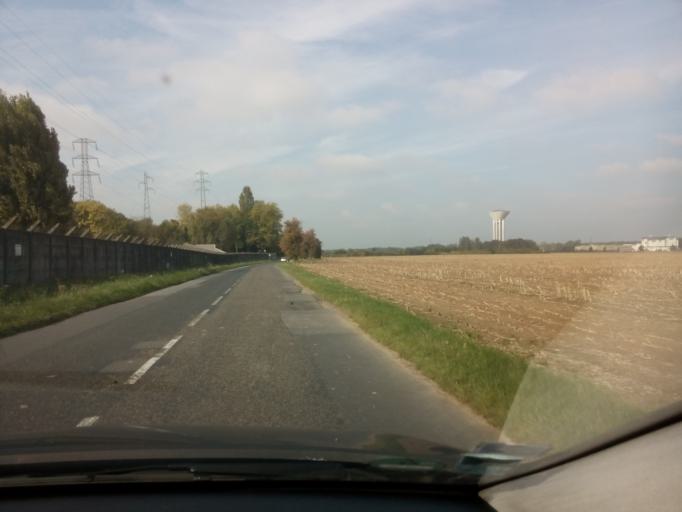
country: FR
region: Ile-de-France
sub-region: Departement des Yvelines
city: Jouy-en-Josas
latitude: 48.7475
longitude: 2.1775
